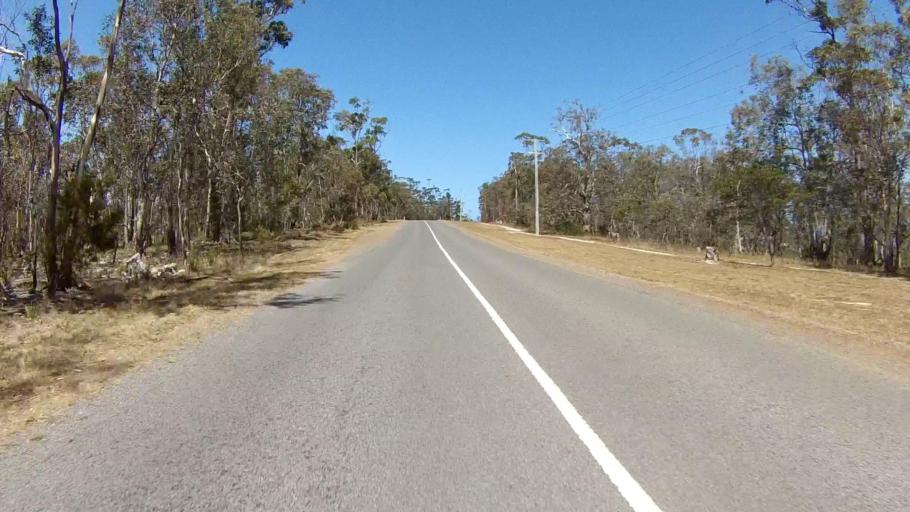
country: AU
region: Tasmania
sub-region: Clarence
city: Sandford
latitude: -43.0029
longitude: 147.4765
